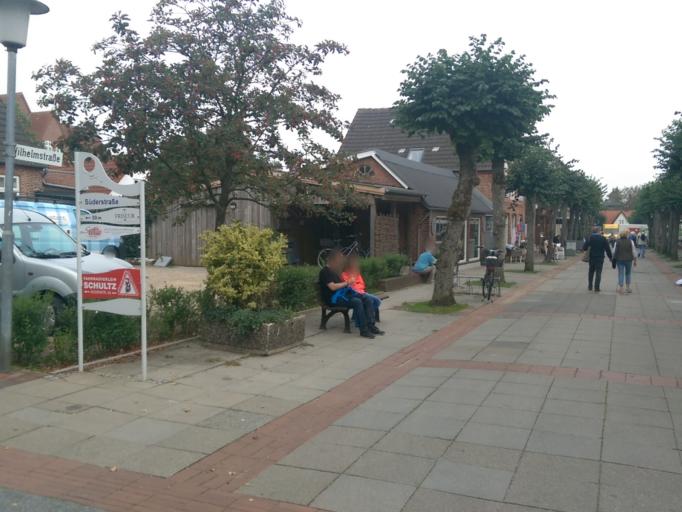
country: DE
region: Schleswig-Holstein
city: Wyk auf Fohr
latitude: 54.6888
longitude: 8.5683
